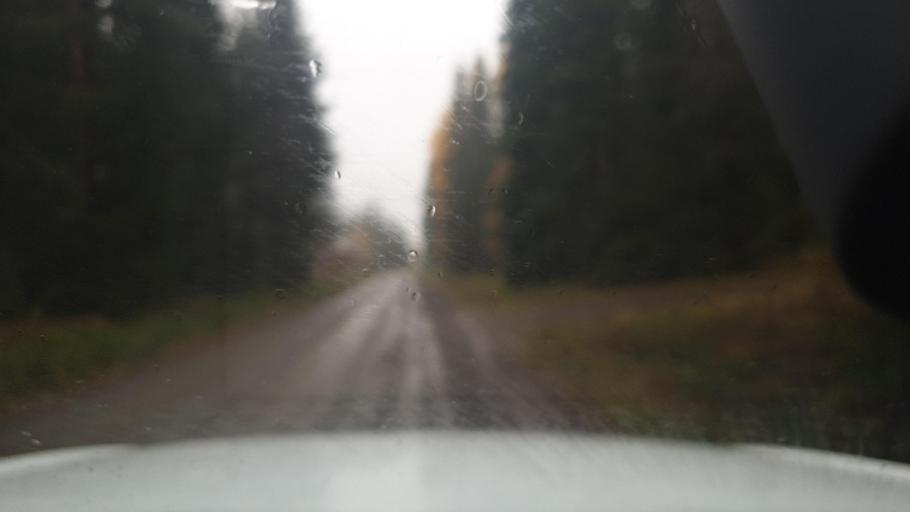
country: SE
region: Vaermland
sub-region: Sunne Kommun
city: Sunne
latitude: 59.8076
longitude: 13.0760
